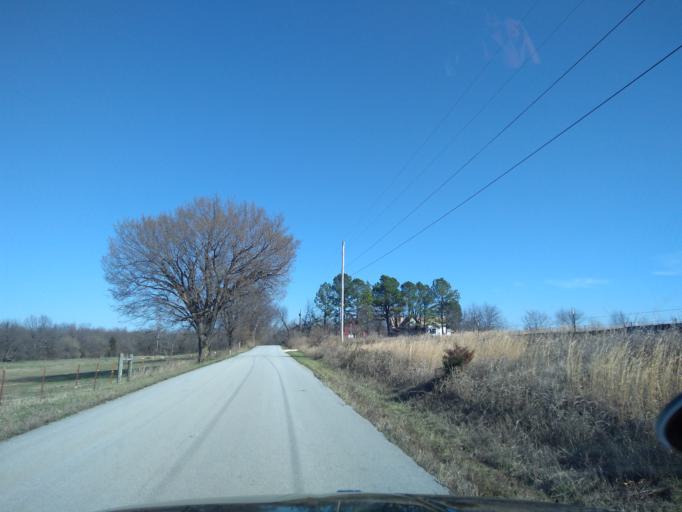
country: US
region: Arkansas
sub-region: Washington County
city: Farmington
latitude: 36.0610
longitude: -94.2441
